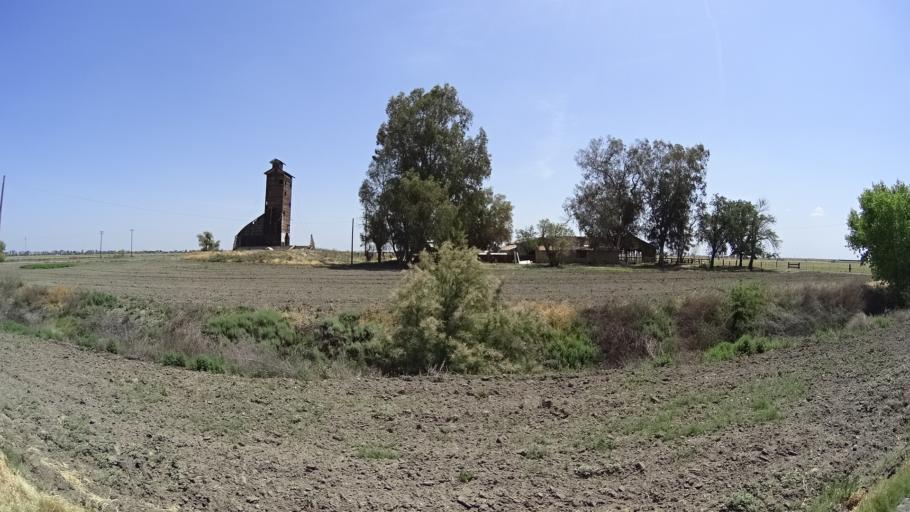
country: US
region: California
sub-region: Kings County
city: Stratford
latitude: 36.1753
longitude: -119.8516
